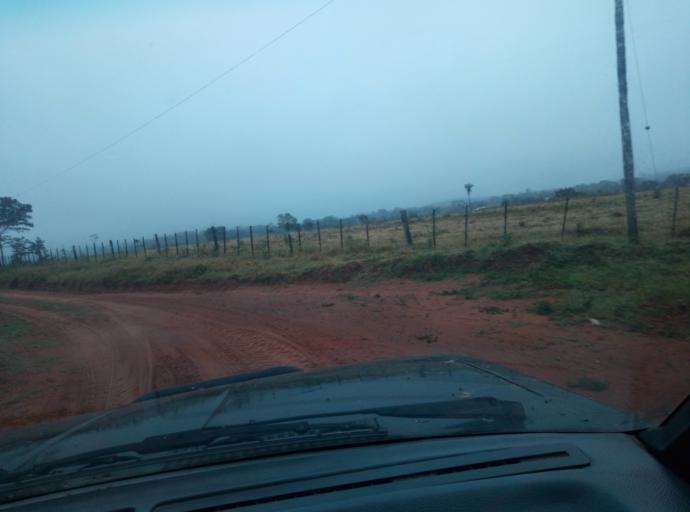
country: PY
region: Caaguazu
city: Carayao
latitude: -25.1906
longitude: -56.3205
